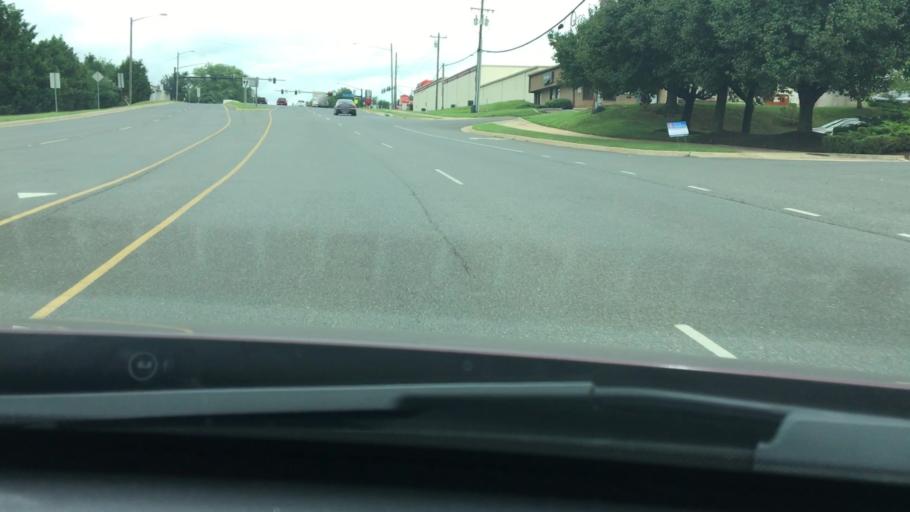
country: US
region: Virginia
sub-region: Prince William County
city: Yorkshire
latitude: 38.7686
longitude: -77.4434
